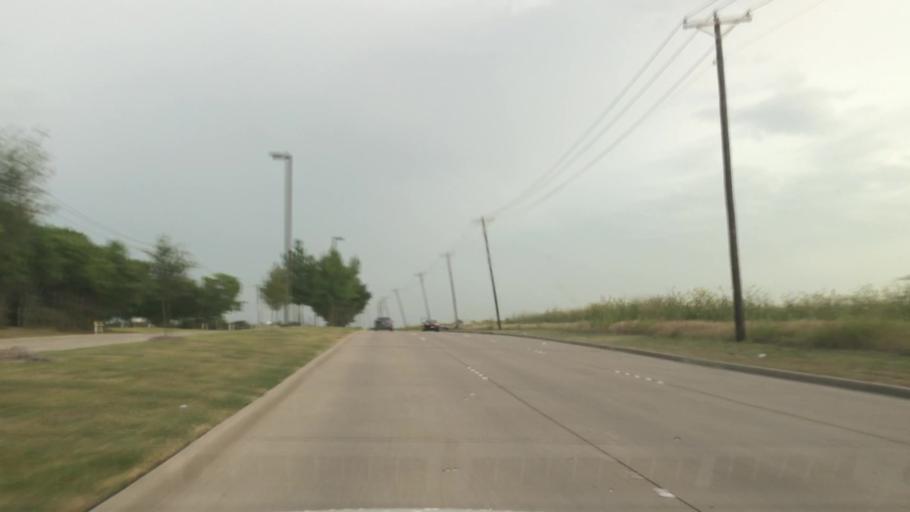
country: US
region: Texas
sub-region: Dallas County
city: Mesquite
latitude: 32.7267
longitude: -96.5499
